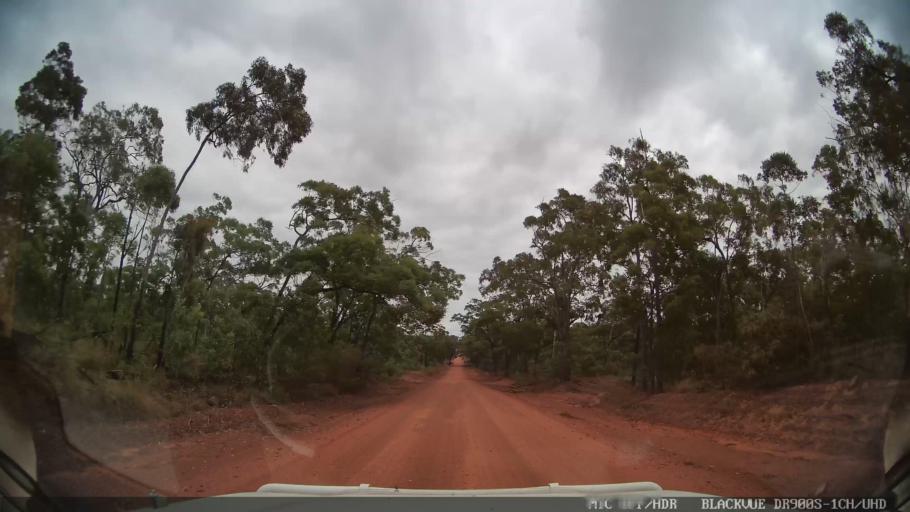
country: AU
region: Queensland
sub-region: Cook
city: Cooktown
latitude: -15.2645
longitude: 144.9527
